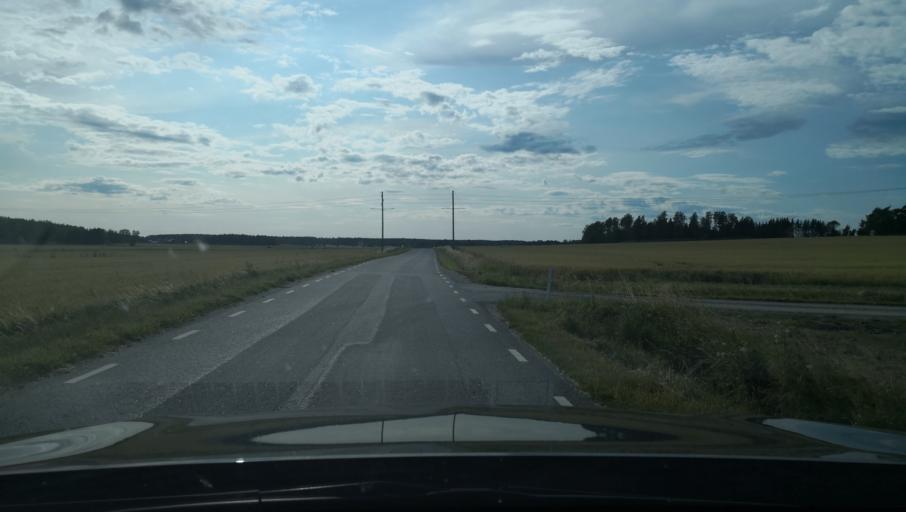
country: SE
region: Uppsala
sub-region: Enkopings Kommun
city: Orsundsbro
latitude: 59.7011
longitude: 17.2912
